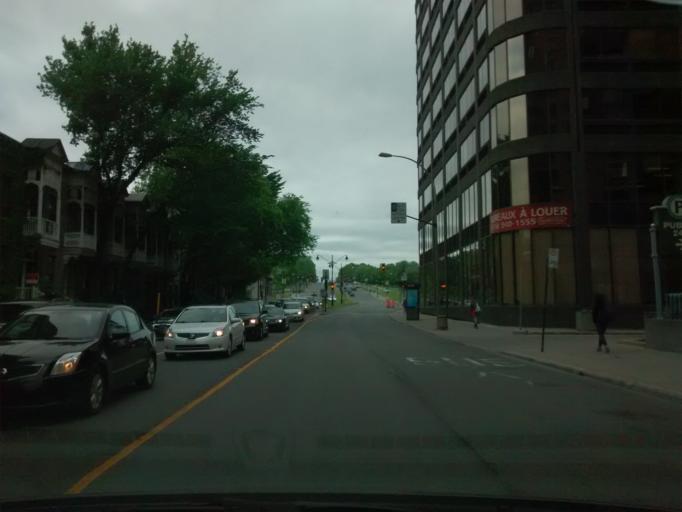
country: CA
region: Quebec
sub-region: Montreal
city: Montreal
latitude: 45.5108
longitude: -73.5762
